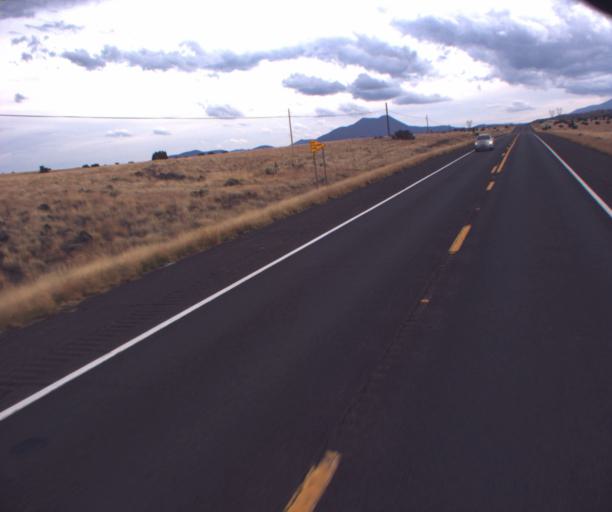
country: US
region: Arizona
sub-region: Coconino County
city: Flagstaff
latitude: 35.5525
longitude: -111.5363
